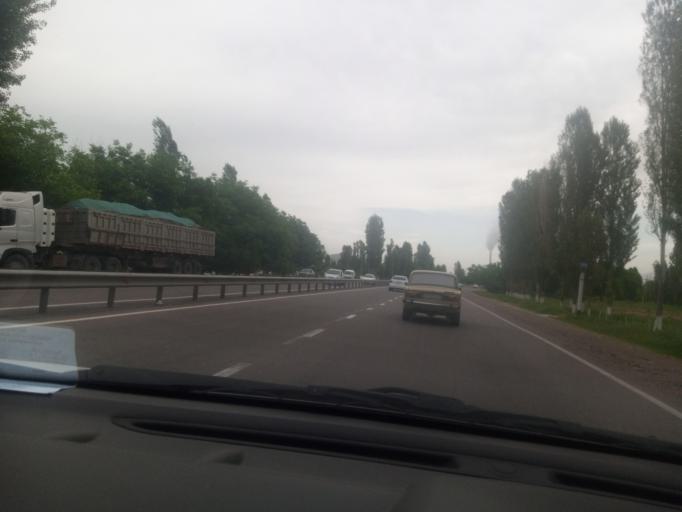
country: UZ
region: Toshkent
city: Ohangaron
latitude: 40.9093
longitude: 69.7480
